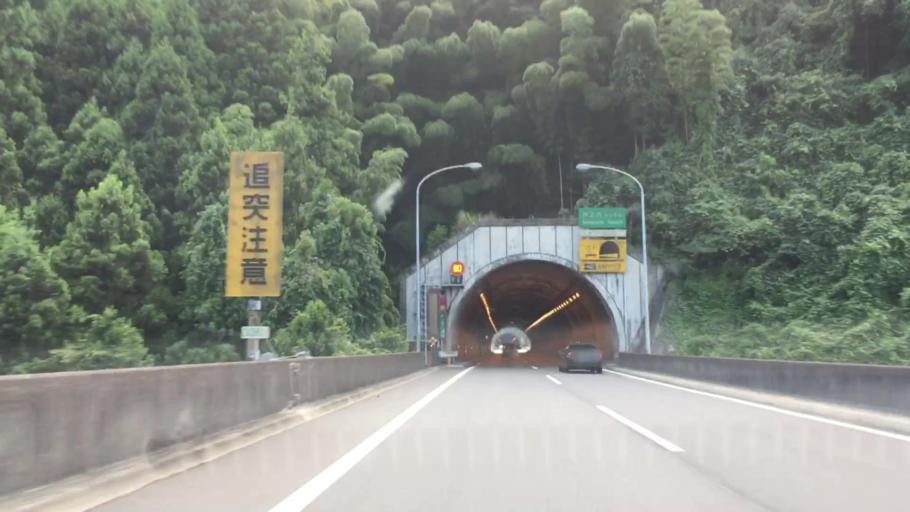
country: JP
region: Yamaguchi
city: Iwakuni
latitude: 34.1535
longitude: 132.1424
